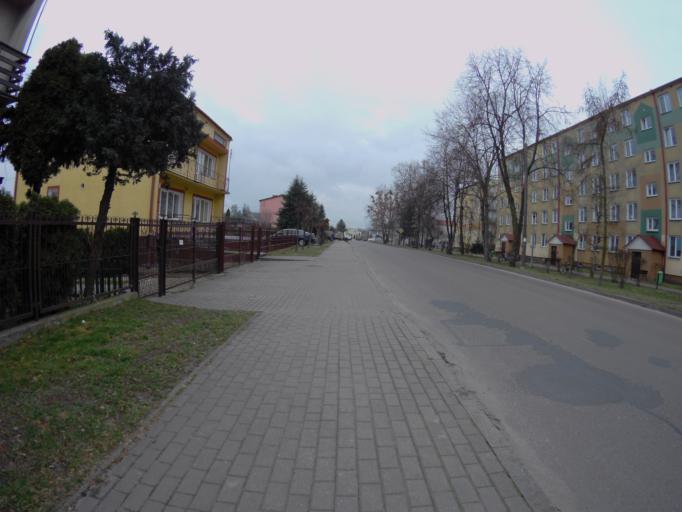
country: PL
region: Lublin Voivodeship
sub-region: Powiat bialski
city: Terespol
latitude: 52.0730
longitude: 23.6044
